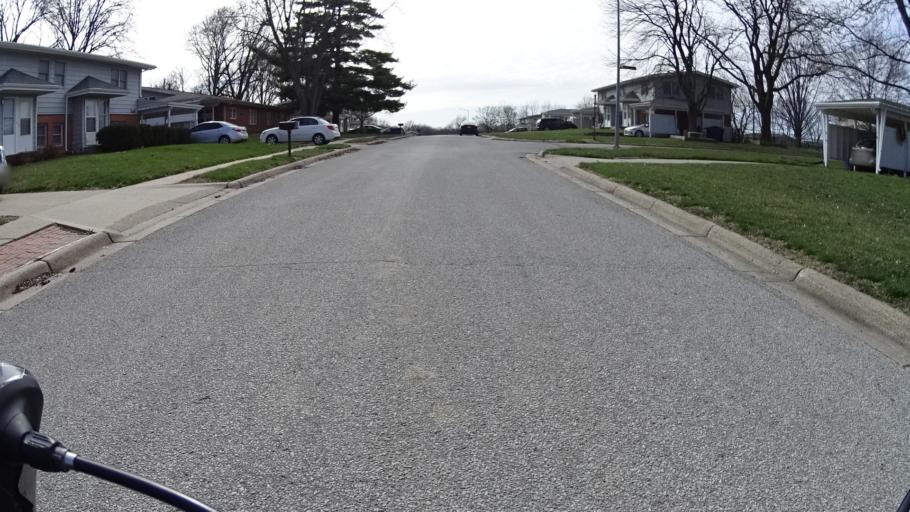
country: US
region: Nebraska
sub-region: Sarpy County
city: Offutt Air Force Base
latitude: 41.1186
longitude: -95.9627
